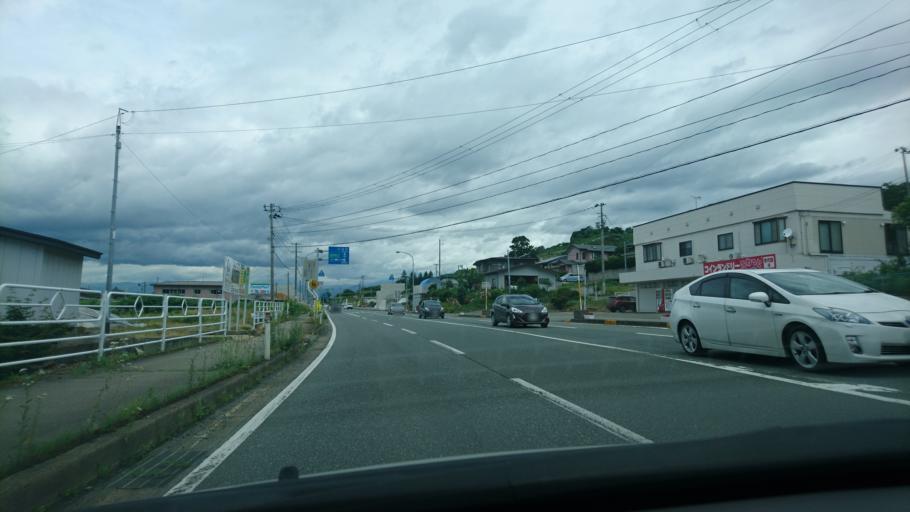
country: JP
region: Iwate
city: Morioka-shi
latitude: 39.6584
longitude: 141.1806
